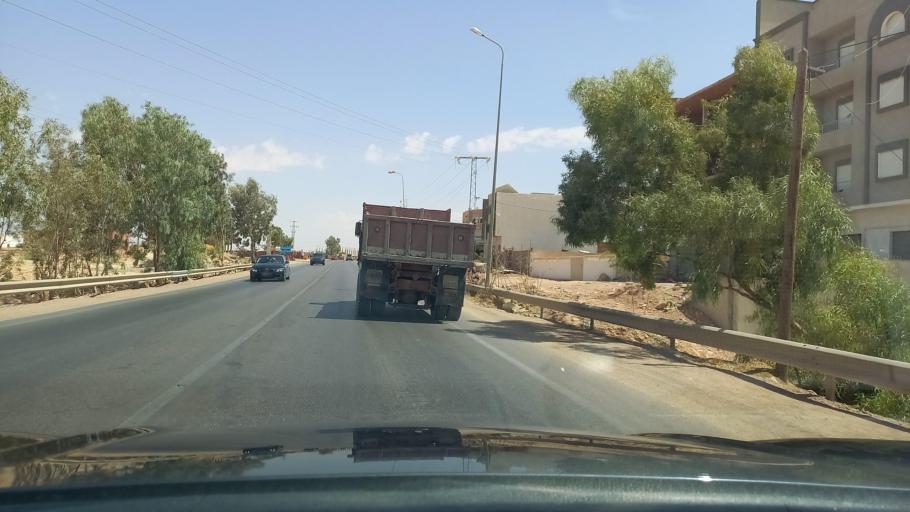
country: TN
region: Madanin
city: Medenine
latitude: 33.3675
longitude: 10.4534
